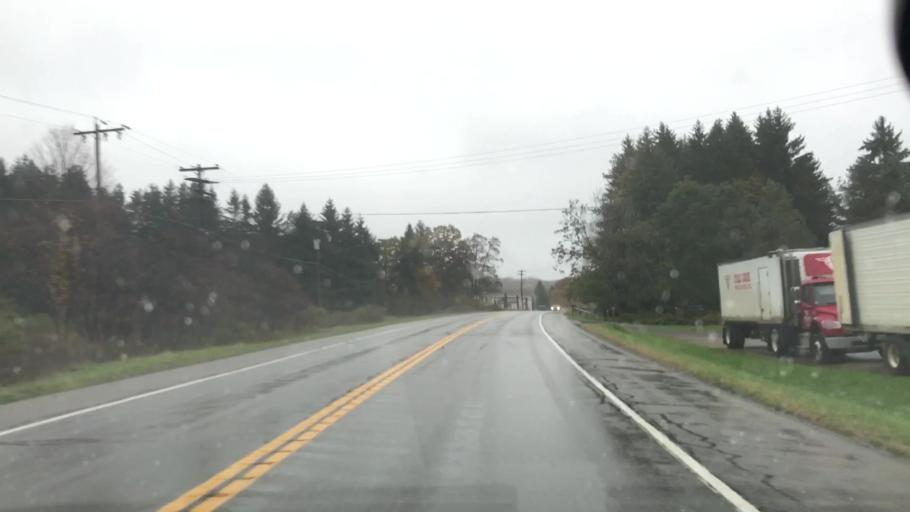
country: US
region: New York
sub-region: Erie County
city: Springville
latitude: 42.3984
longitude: -78.6781
